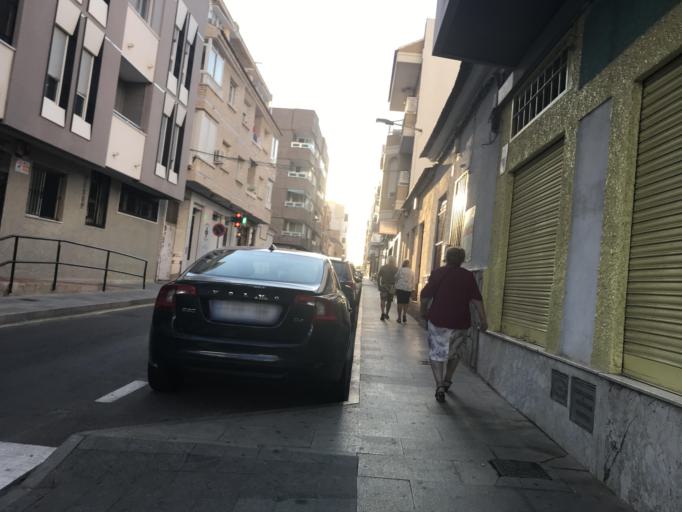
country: ES
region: Valencia
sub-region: Provincia de Alicante
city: Torrevieja
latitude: 37.9791
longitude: -0.6817
